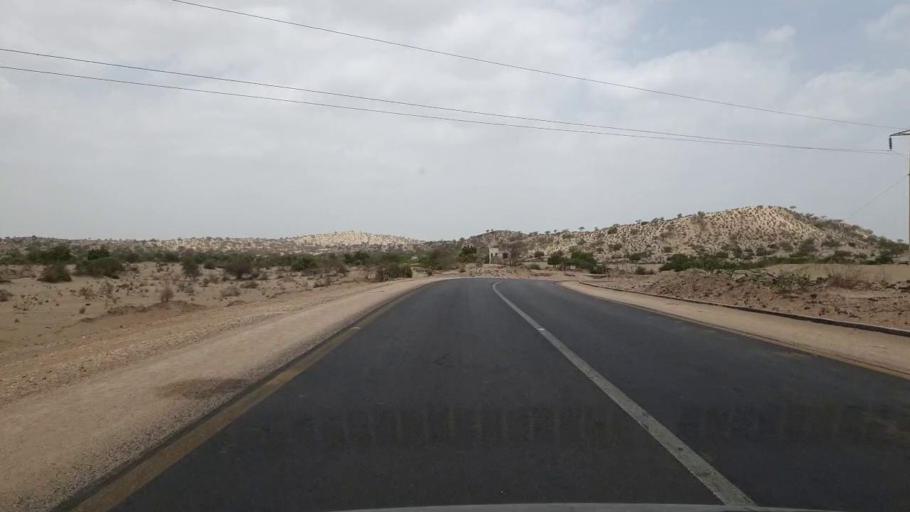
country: PK
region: Sindh
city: Naukot
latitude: 24.8352
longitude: 69.4734
